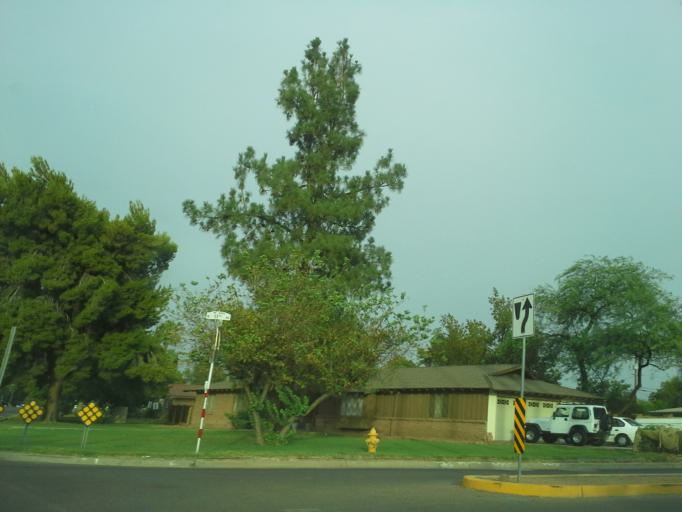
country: US
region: Arizona
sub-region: Maricopa County
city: Glendale
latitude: 33.5602
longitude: -112.0871
